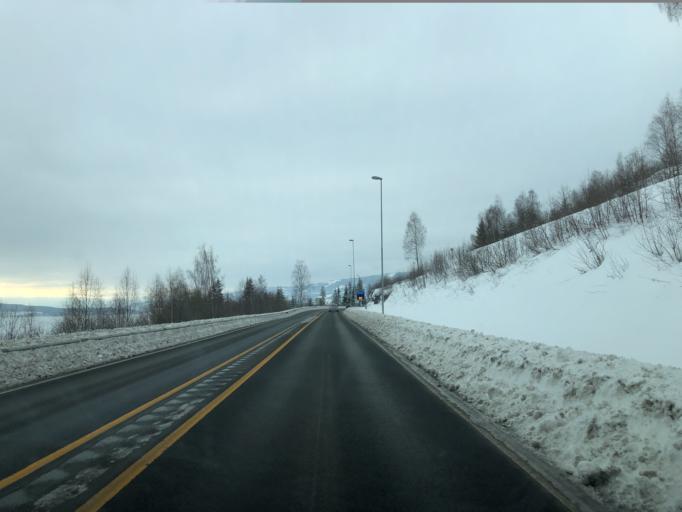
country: NO
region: Oppland
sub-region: Lillehammer
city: Lillehammer
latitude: 61.0569
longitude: 10.4325
